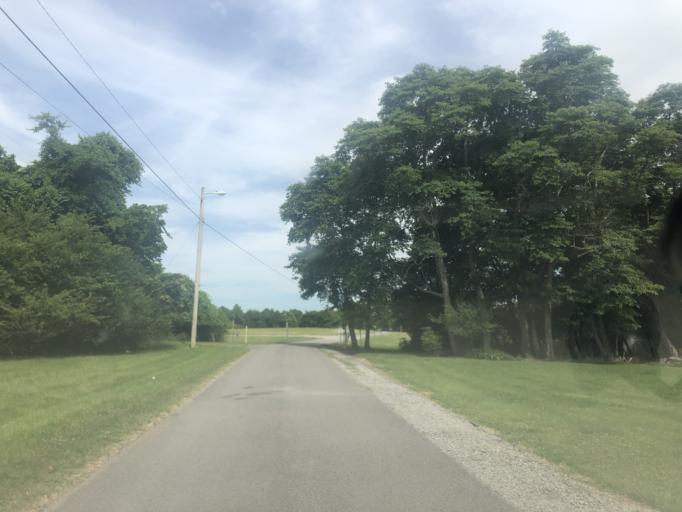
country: US
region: Tennessee
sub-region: Davidson County
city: Lakewood
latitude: 36.2035
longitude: -86.6601
